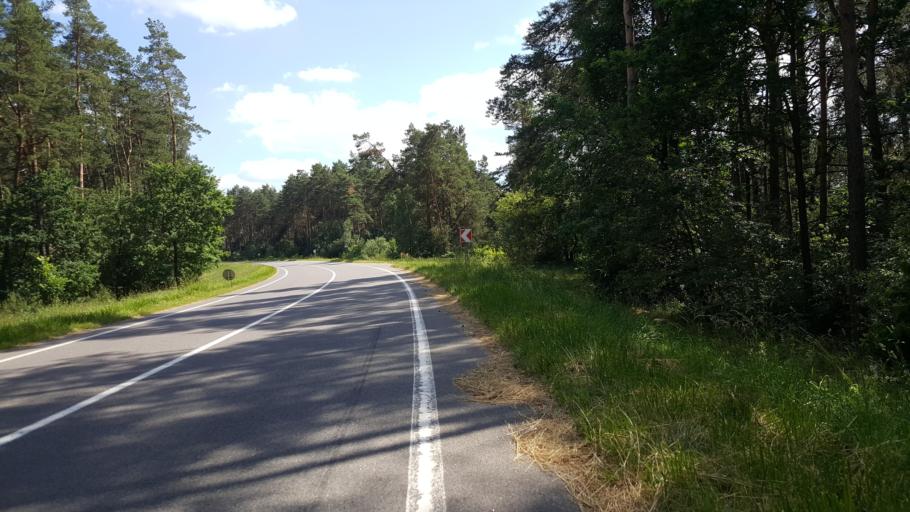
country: BY
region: Brest
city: Kamyanyuki
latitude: 52.5068
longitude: 23.6600
